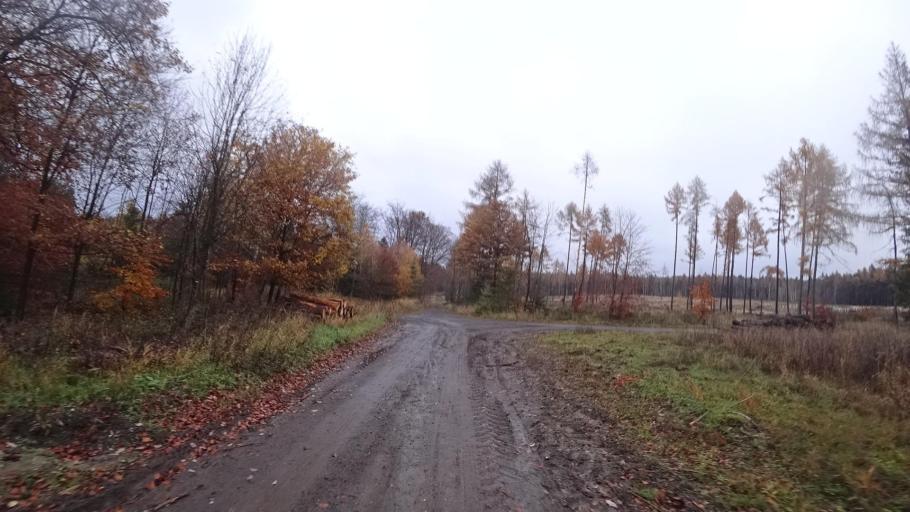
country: DE
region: Rheinland-Pfalz
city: Schalkenbach
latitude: 50.5031
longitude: 7.1209
